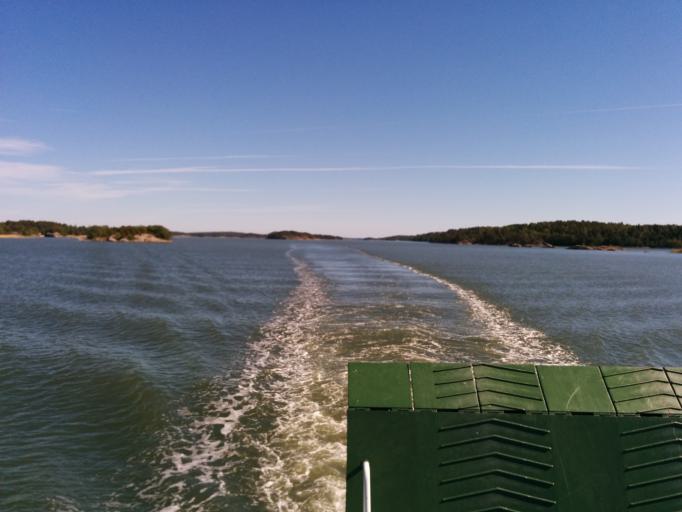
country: FI
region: Varsinais-Suomi
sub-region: Turku
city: Velkua
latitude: 60.4563
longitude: 21.7013
